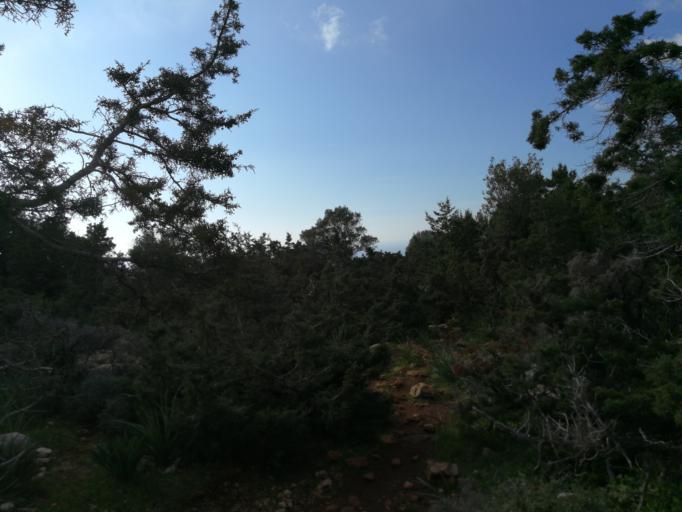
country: CY
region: Pafos
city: Pegeia
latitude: 34.9248
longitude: 32.3566
